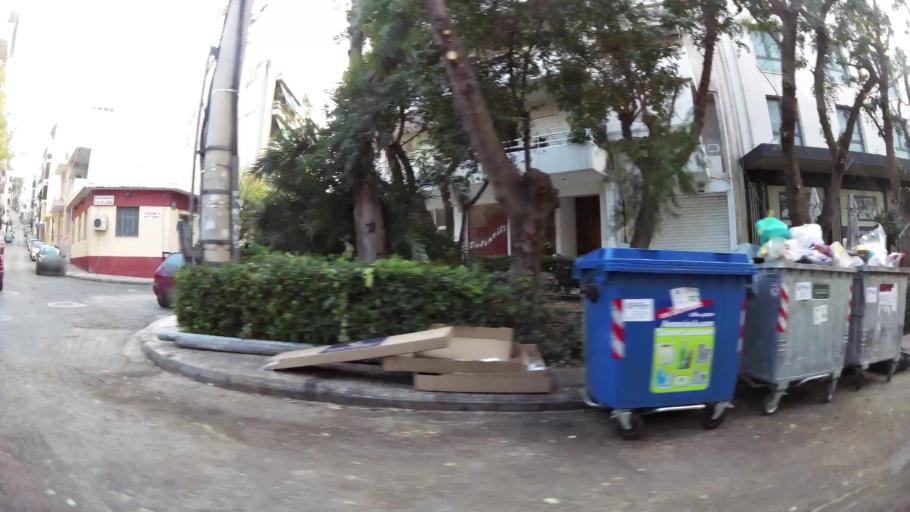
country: GR
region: Attica
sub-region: Nomarchia Athinas
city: Dhafni
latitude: 37.9575
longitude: 23.7300
